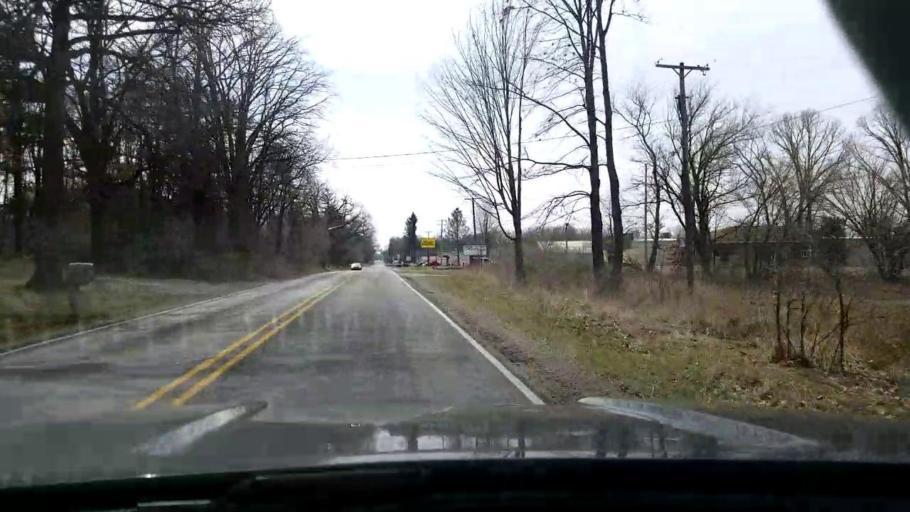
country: US
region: Michigan
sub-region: Jackson County
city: Spring Arbor
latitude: 42.1558
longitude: -84.5190
